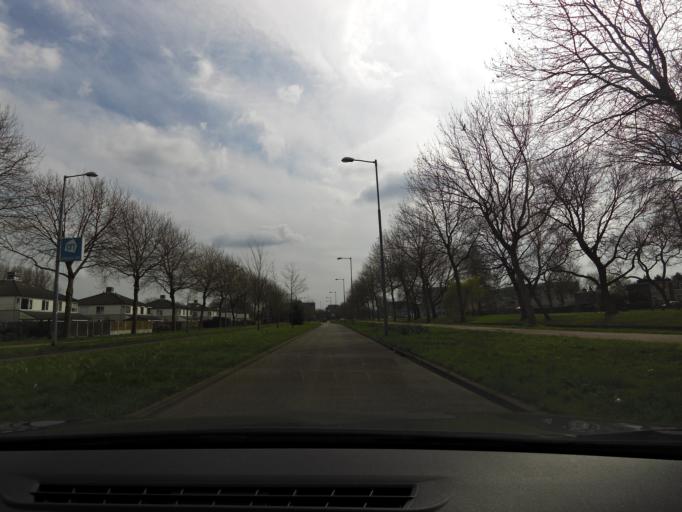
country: NL
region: South Holland
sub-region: Gemeente Spijkenisse
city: Spijkenisse
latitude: 51.8590
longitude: 4.3576
